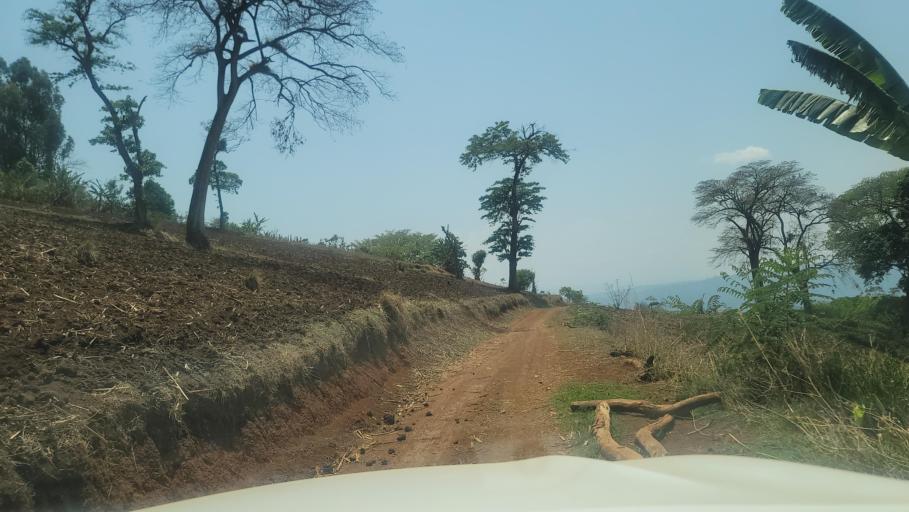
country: ET
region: Southern Nations, Nationalities, and People's Region
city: Bonga
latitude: 7.5317
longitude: 36.1899
